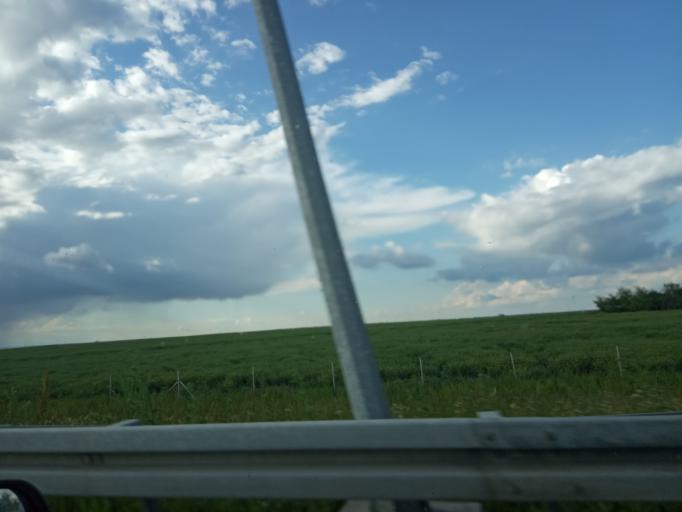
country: RS
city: Dobanovci
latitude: 44.8373
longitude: 20.2565
